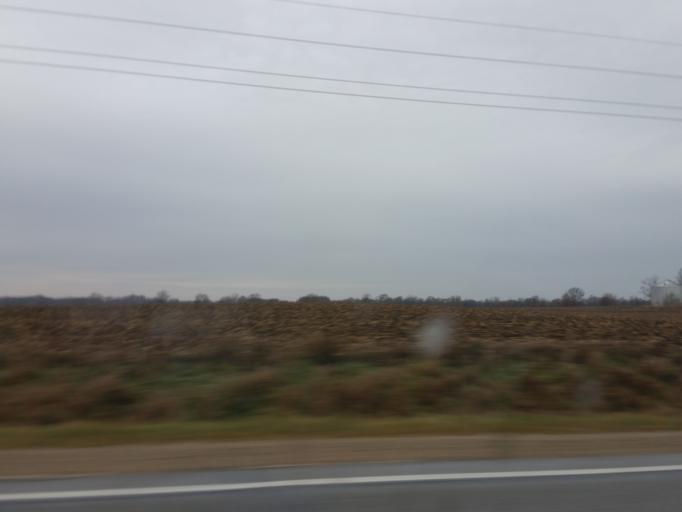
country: US
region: Iowa
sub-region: Black Hawk County
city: La Porte City
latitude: 42.3811
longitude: -92.2442
